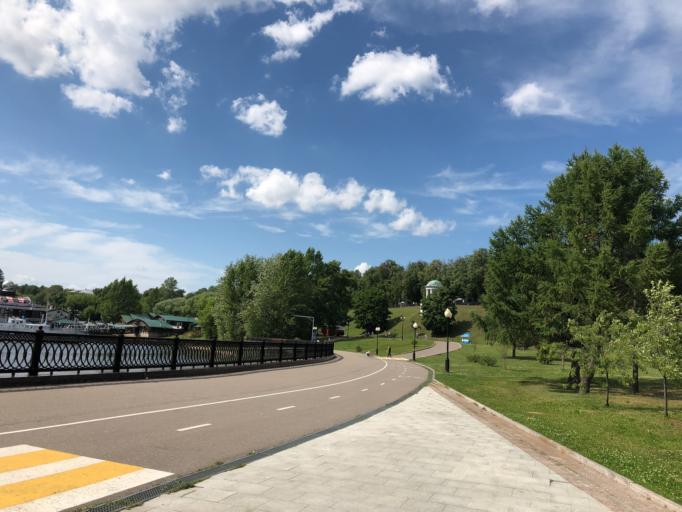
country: RU
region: Jaroslavl
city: Yaroslavl
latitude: 57.6201
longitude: 39.9034
